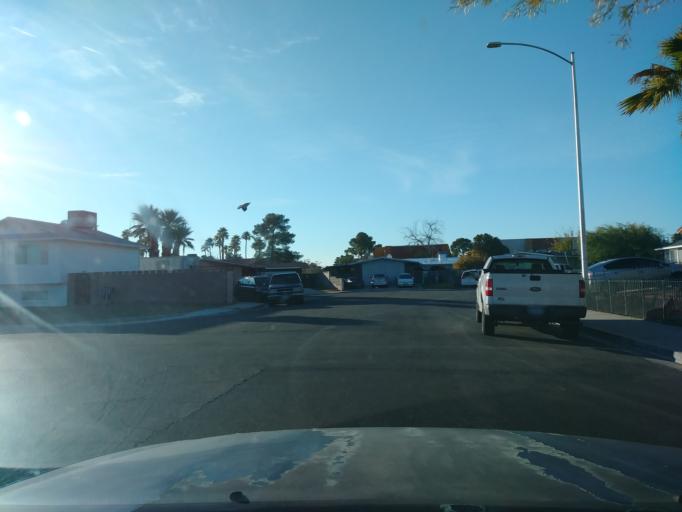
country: US
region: Nevada
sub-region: Clark County
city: Spring Valley
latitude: 36.1630
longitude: -115.2415
